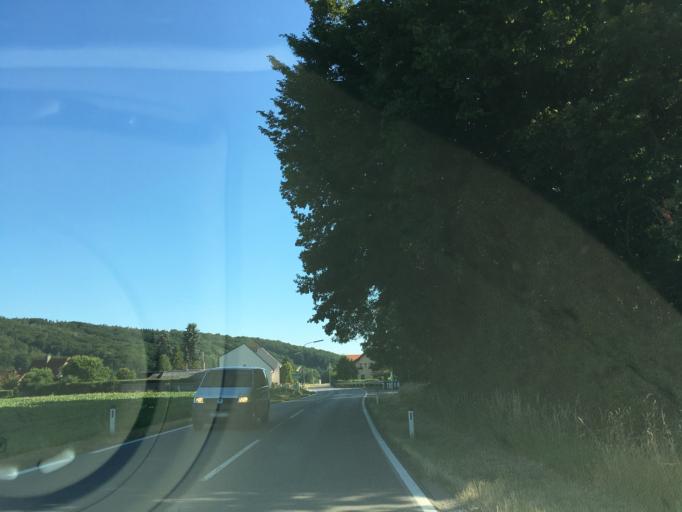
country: AT
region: Lower Austria
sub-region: Politischer Bezirk Sankt Polten
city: Boheimkirchen
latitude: 48.1809
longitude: 15.7592
